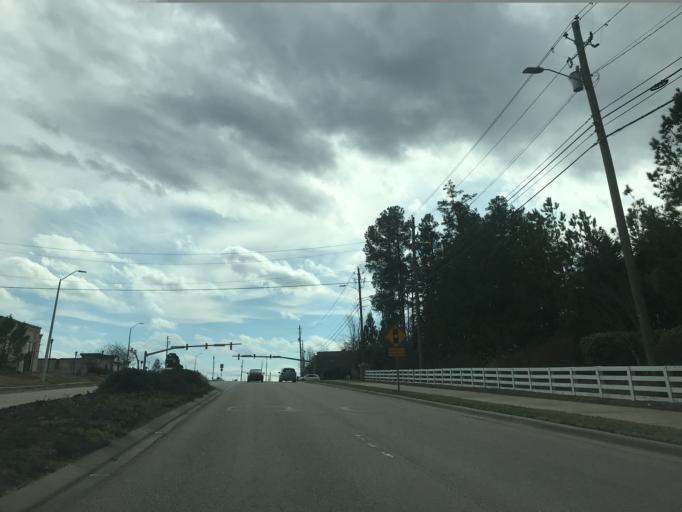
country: US
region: North Carolina
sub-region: Wake County
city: Morrisville
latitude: 35.7951
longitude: -78.8478
